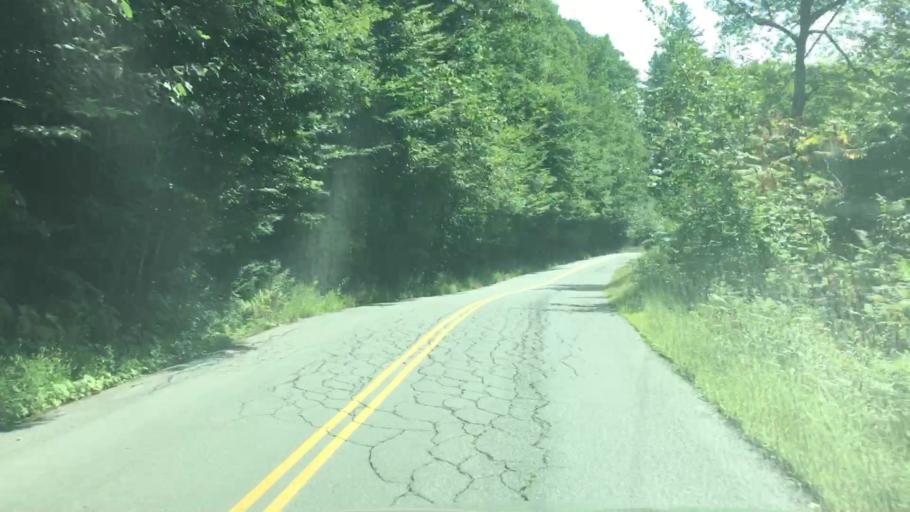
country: US
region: Vermont
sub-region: Windham County
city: West Brattleboro
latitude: 42.8006
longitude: -72.6858
